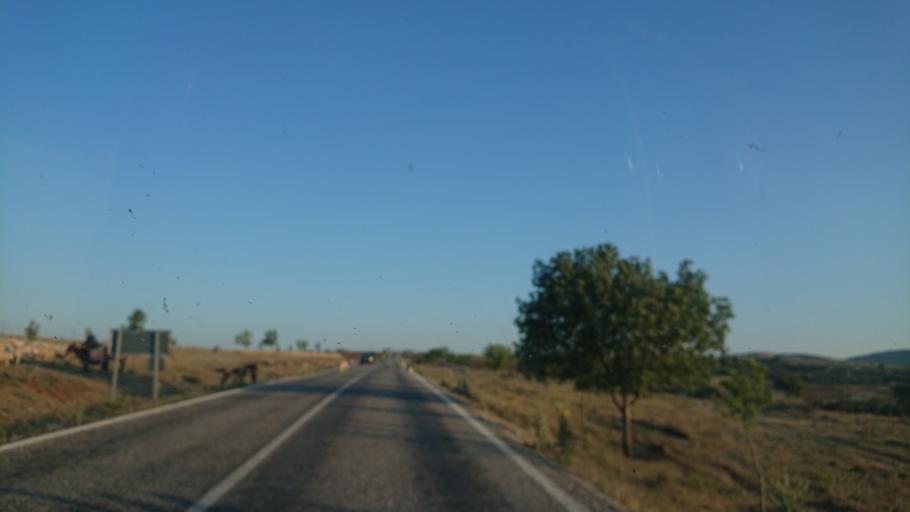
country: TR
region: Aksaray
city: Sariyahsi
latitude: 38.9564
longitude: 33.8379
